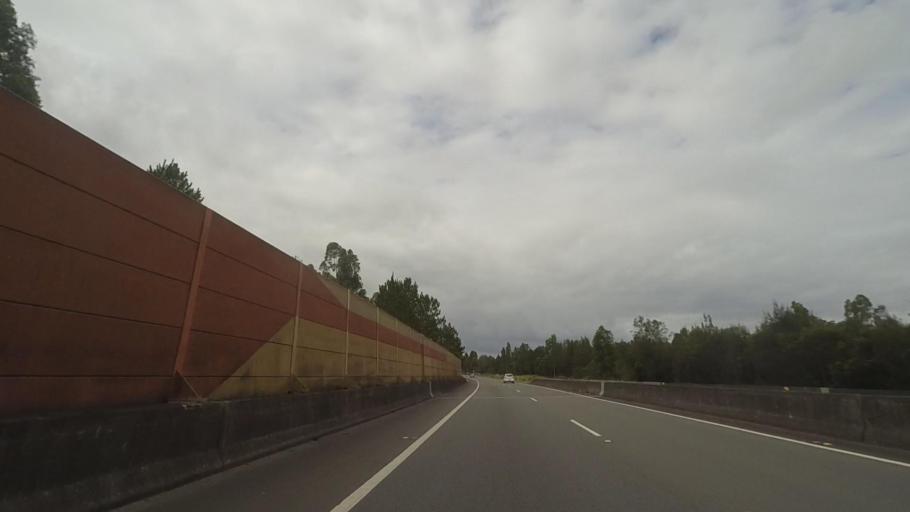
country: AU
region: New South Wales
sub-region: Port Stephens Shire
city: Raymond Terrace
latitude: -32.7690
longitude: 151.7619
